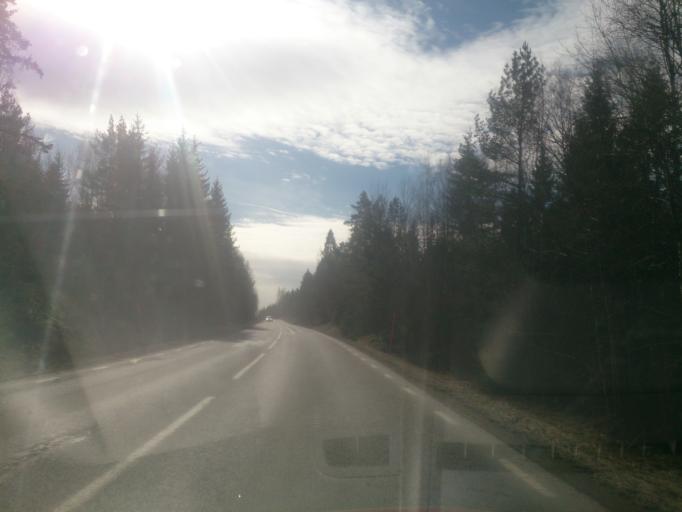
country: SE
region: OEstergoetland
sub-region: Finspangs Kommun
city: Finspang
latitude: 58.6165
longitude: 15.8112
